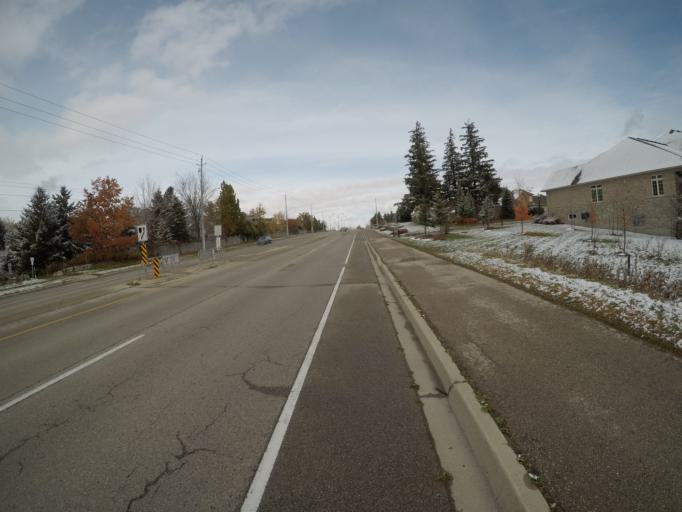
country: CA
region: Ontario
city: Waterloo
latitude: 43.5087
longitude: -80.4974
